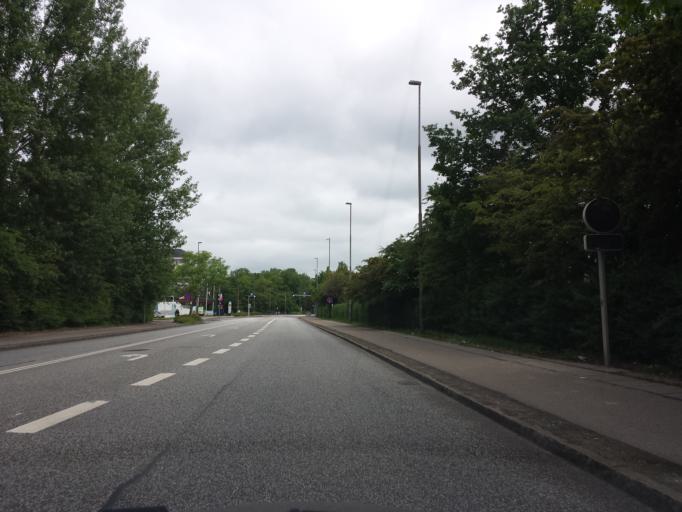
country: DK
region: Capital Region
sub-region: Ballerup Kommune
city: Ballerup
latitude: 55.7255
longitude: 12.3461
